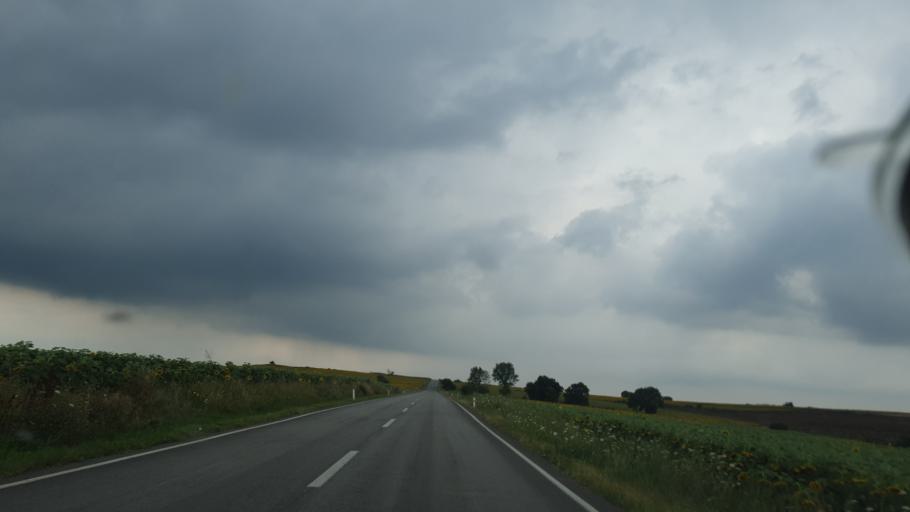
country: TR
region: Kirklareli
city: Pehlivankoy
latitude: 41.2179
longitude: 26.9695
